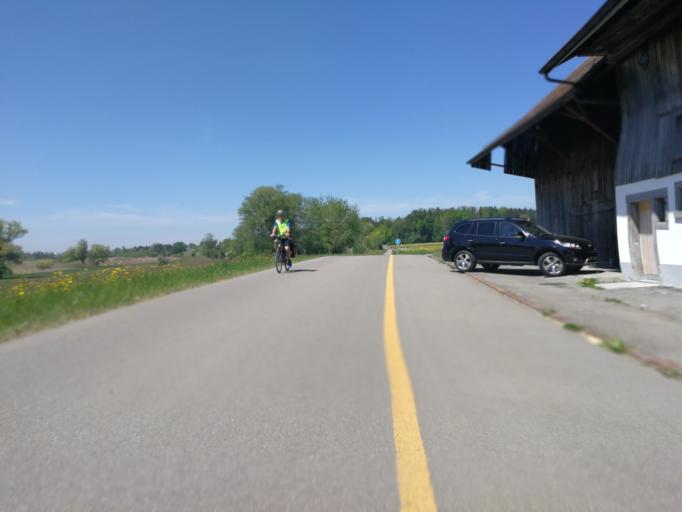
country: CH
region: Zurich
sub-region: Bezirk Uster
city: Greifensee
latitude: 47.3681
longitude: 8.6717
